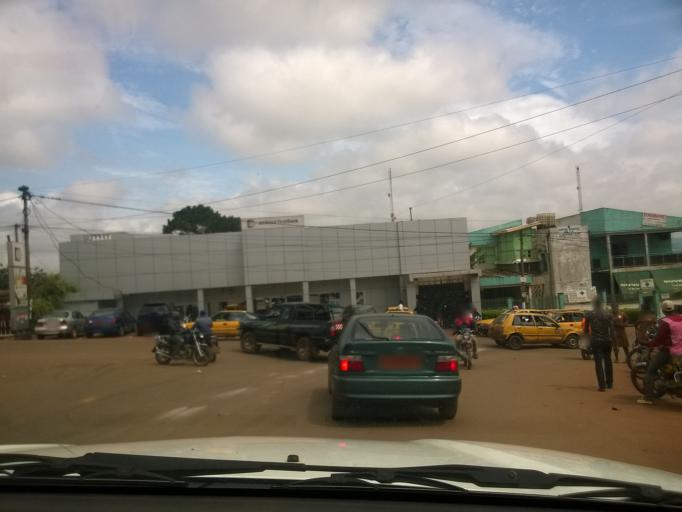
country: CM
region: Centre
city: Yaounde
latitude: 3.8689
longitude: 11.5498
